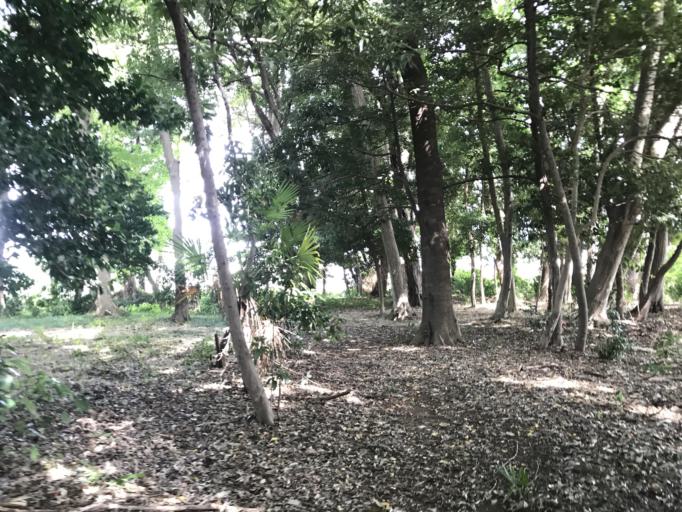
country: JP
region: Tokyo
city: Tanashicho
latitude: 35.7777
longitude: 139.5508
